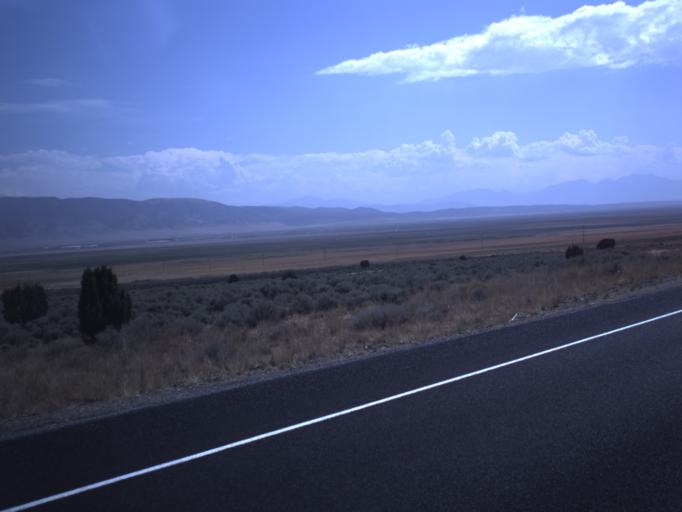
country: US
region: Utah
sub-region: Utah County
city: Eagle Mountain
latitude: 40.3101
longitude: -112.1017
